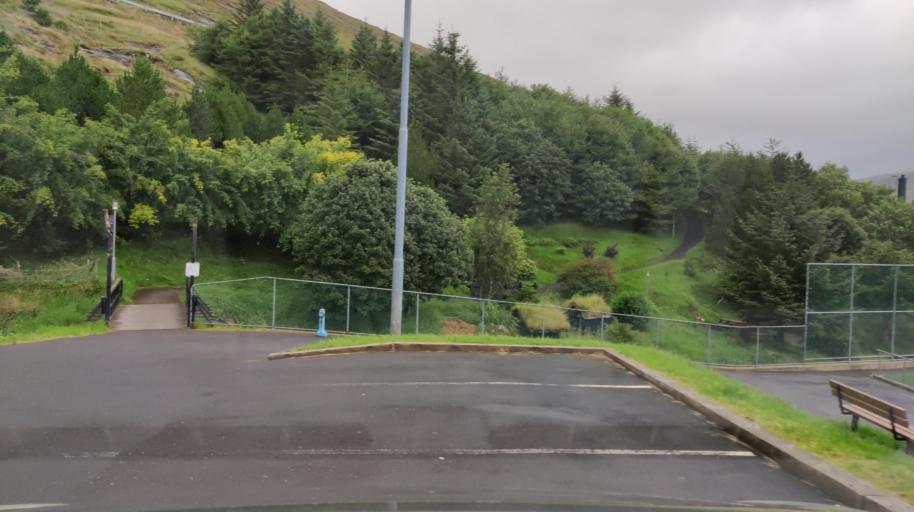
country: FO
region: Streymoy
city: Vestmanna
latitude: 62.1560
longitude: -7.1719
